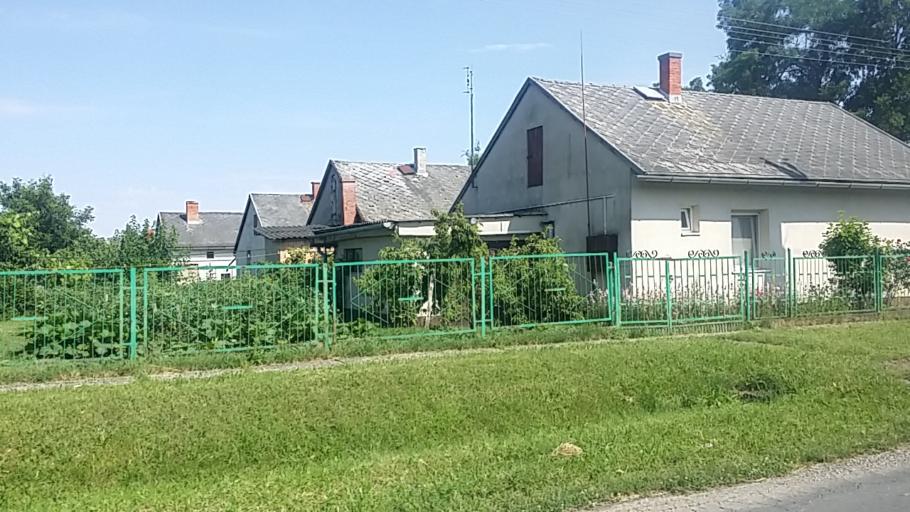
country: HU
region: Fejer
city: Ivancsa
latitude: 47.1806
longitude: 18.8235
